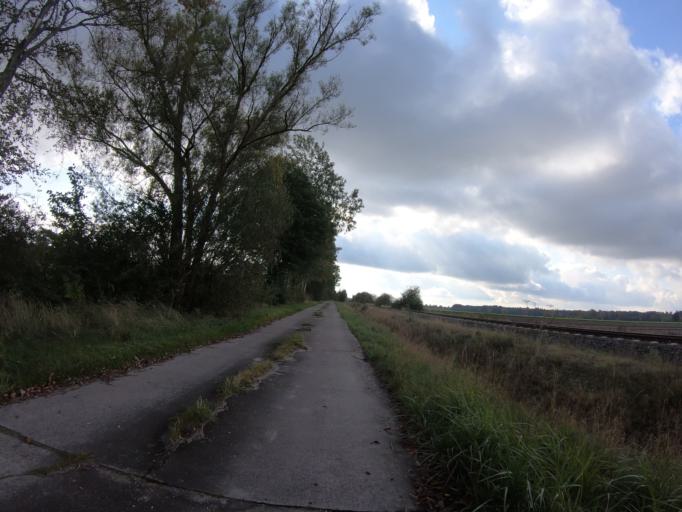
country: DE
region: Lower Saxony
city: Wahrenholz
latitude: 52.5844
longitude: 10.6099
